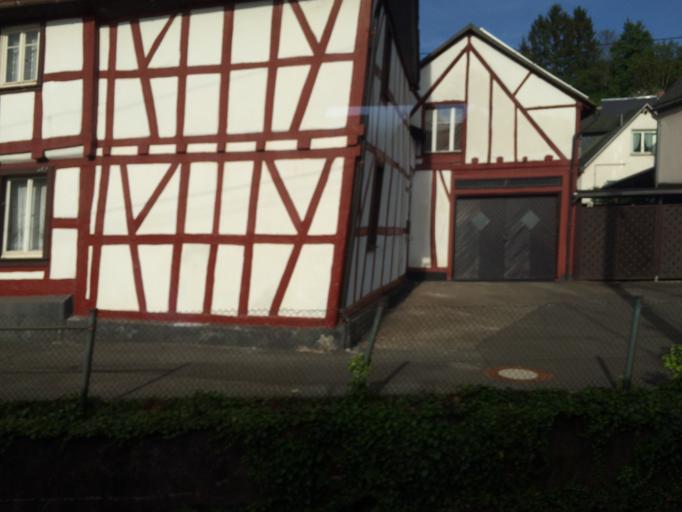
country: DE
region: Rheinland-Pfalz
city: Filsen
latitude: 50.2379
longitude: 7.5836
